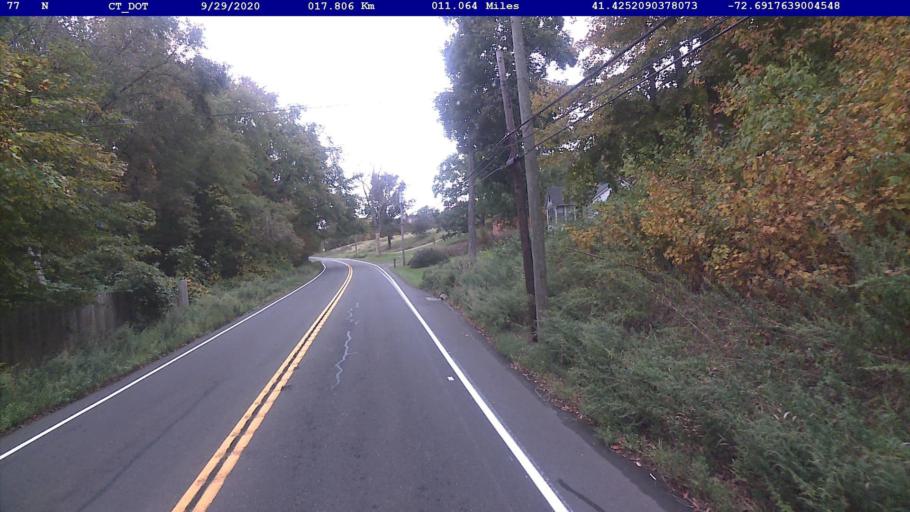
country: US
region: Connecticut
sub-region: Middlesex County
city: Durham
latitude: 41.4252
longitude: -72.6918
